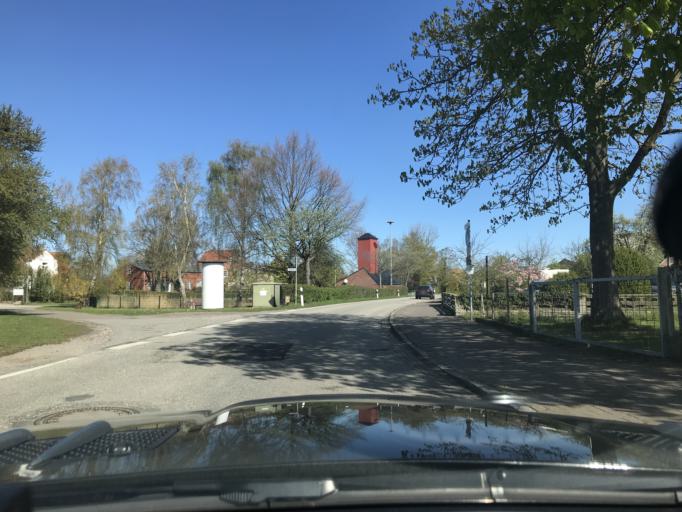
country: DE
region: Schleswig-Holstein
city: Grossenbrode
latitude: 54.4583
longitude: 11.0434
